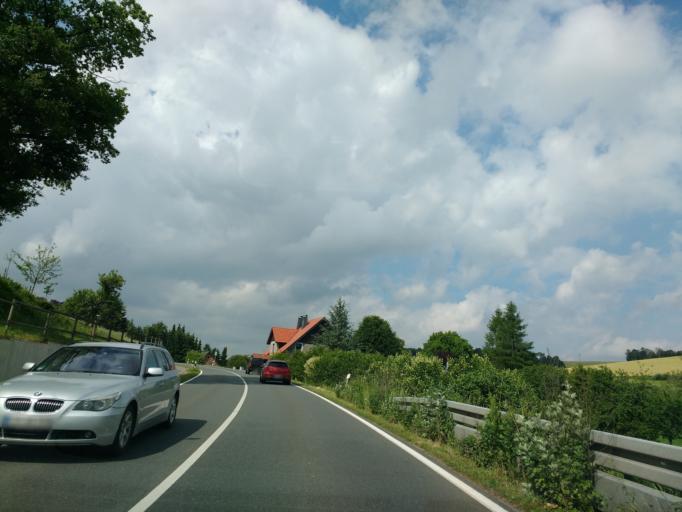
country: DE
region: North Rhine-Westphalia
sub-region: Regierungsbezirk Detmold
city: Lemgo
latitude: 52.0751
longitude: 8.9303
